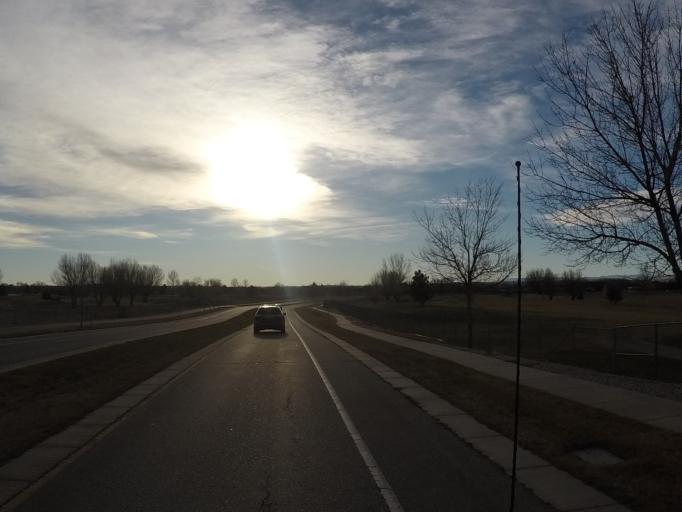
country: US
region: Montana
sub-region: Yellowstone County
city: Billings
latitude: 45.7801
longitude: -108.5991
